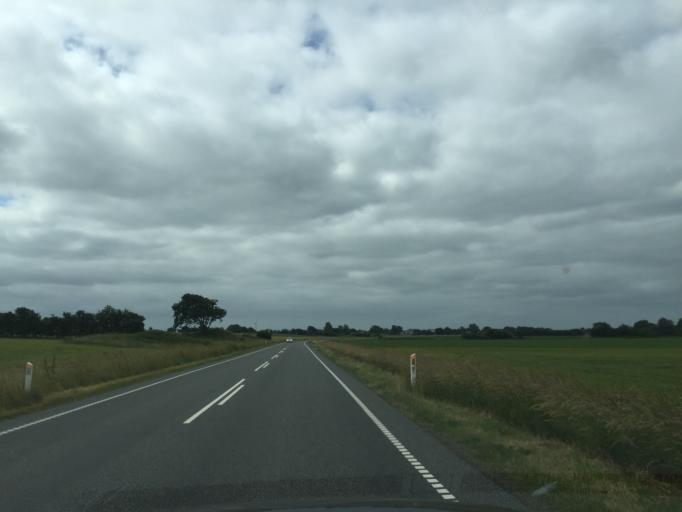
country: DK
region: South Denmark
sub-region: Vejen Kommune
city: Holsted
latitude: 55.4111
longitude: 8.9413
